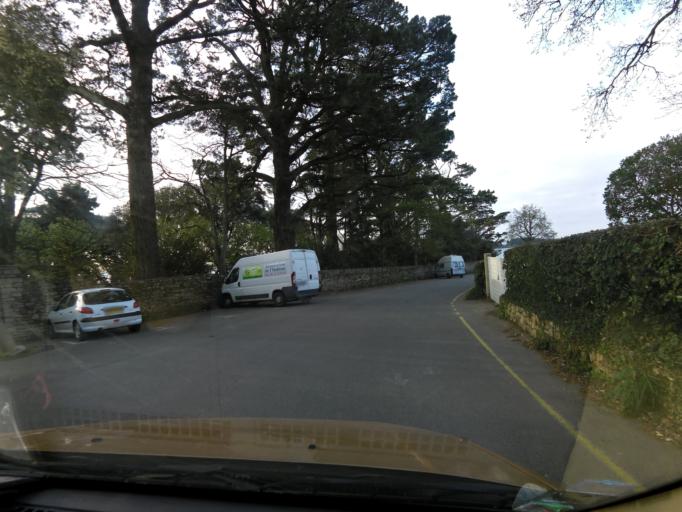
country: FR
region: Brittany
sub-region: Departement du Morbihan
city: Arradon
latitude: 47.6231
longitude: -2.8130
